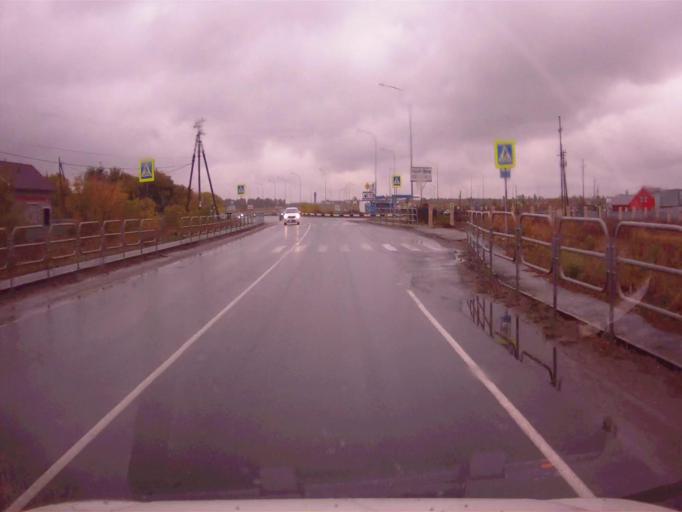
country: RU
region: Chelyabinsk
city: Roshchino
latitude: 55.3688
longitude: 61.1851
